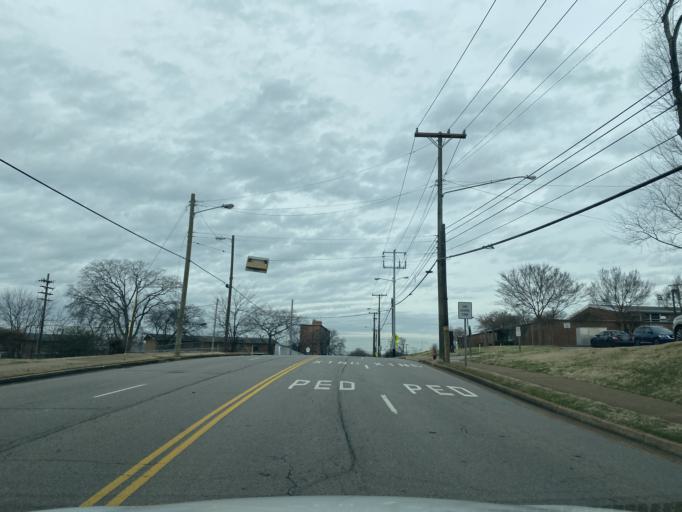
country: US
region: Tennessee
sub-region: Davidson County
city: Nashville
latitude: 36.1418
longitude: -86.7827
